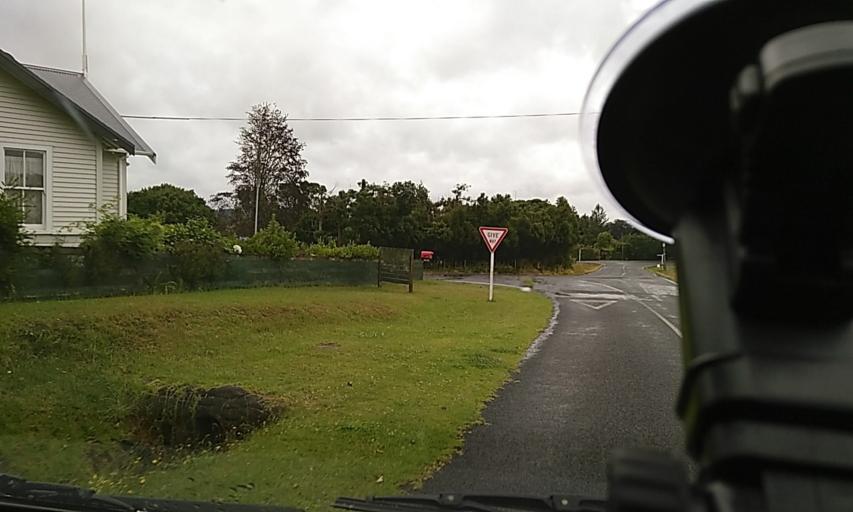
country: NZ
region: Auckland
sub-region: Auckland
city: Pukekohe East
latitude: -37.3291
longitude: 174.9148
